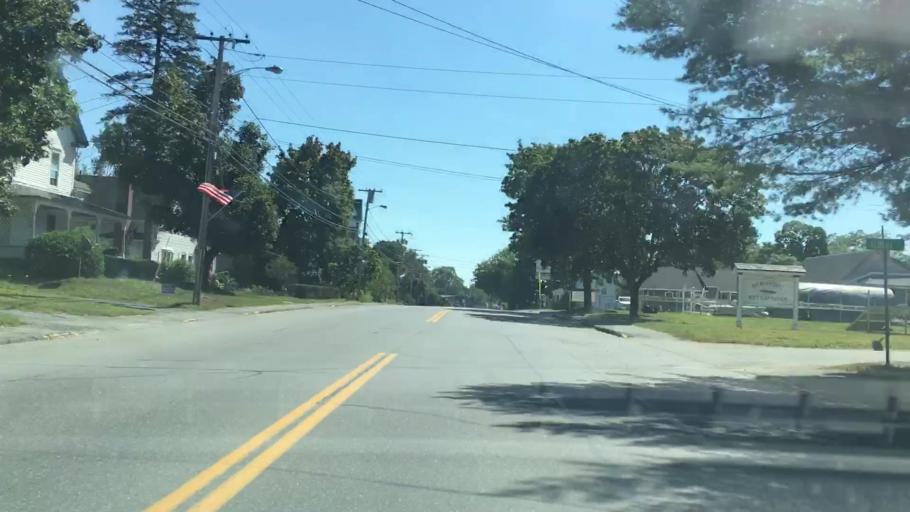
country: US
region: Maine
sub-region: Piscataquis County
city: Milo
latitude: 45.2555
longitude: -68.9868
